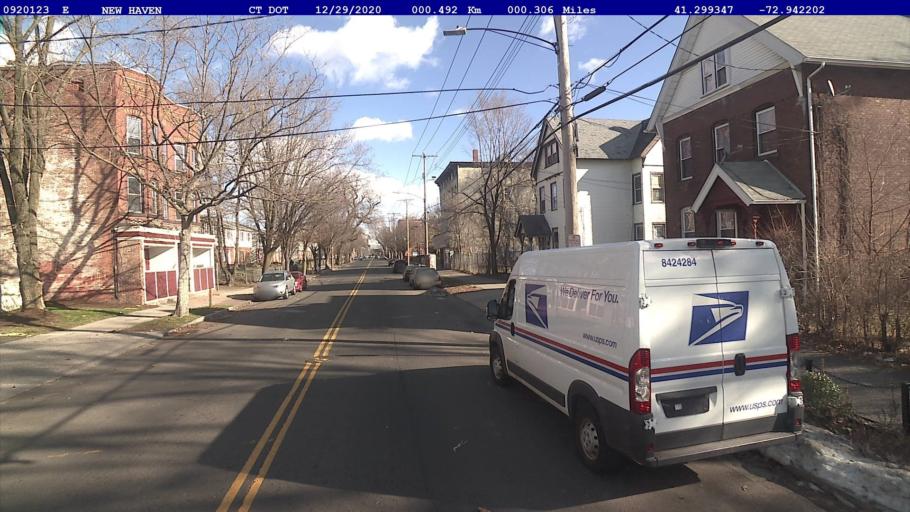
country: US
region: Connecticut
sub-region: New Haven County
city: New Haven
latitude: 41.2993
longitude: -72.9422
